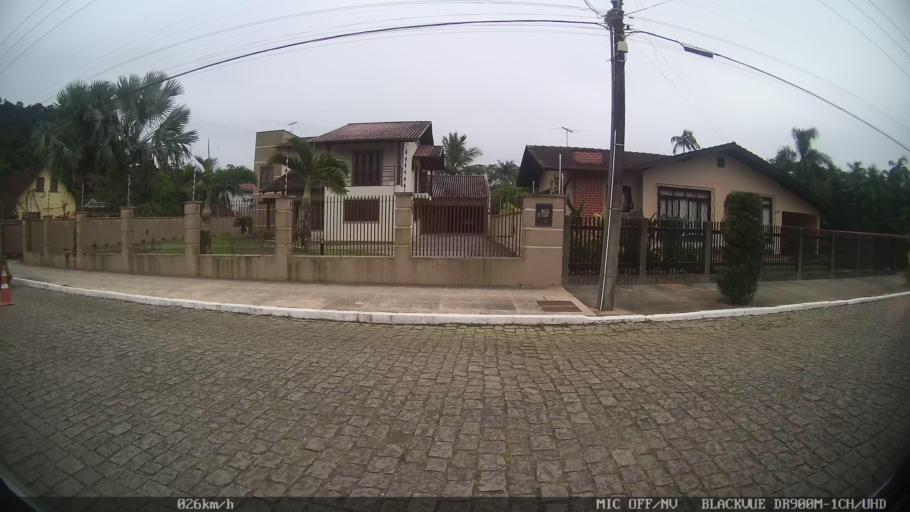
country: BR
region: Santa Catarina
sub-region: Joinville
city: Joinville
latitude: -26.2073
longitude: -48.9129
